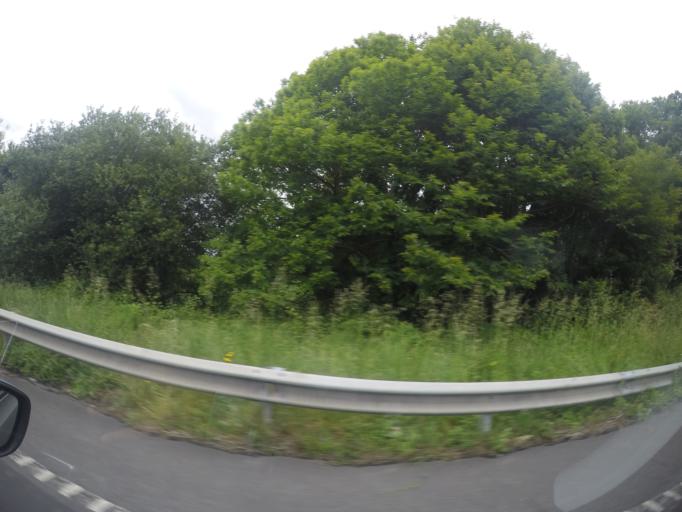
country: ES
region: Galicia
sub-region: Provincia da Coruna
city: Culleredo
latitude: 43.3060
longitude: -8.3800
